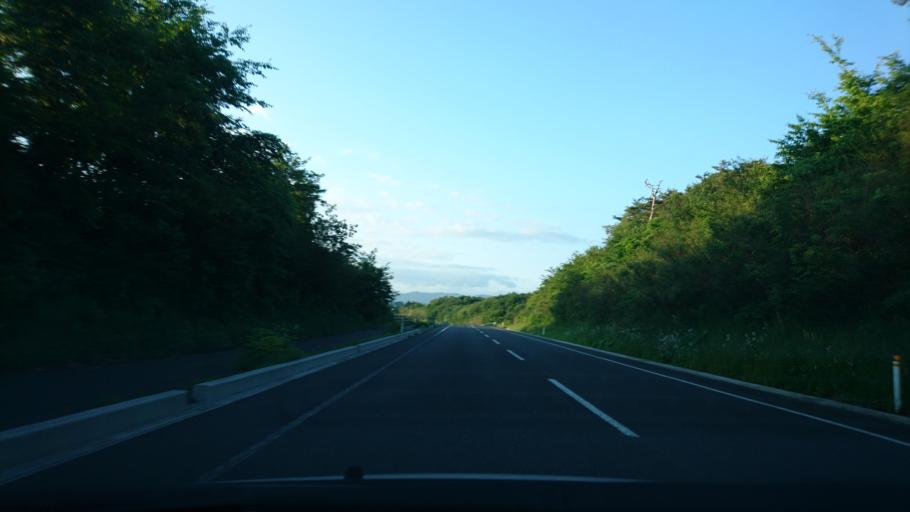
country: JP
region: Iwate
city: Ichinoseki
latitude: 38.9053
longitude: 141.1573
